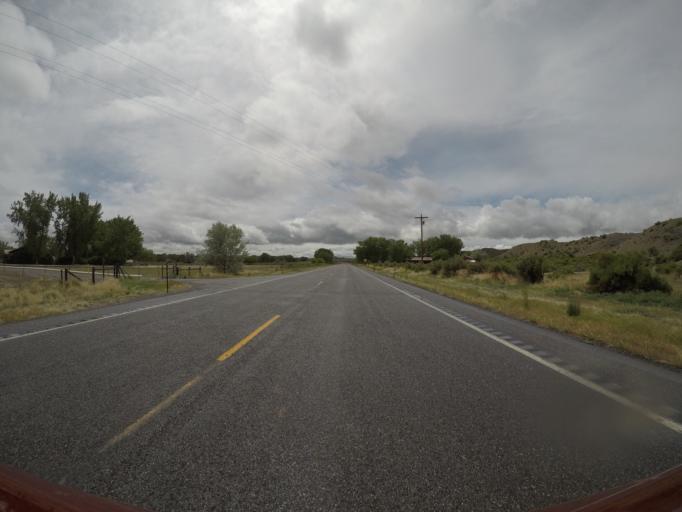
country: US
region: Wyoming
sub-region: Big Horn County
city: Lovell
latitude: 44.8686
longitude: -108.3236
